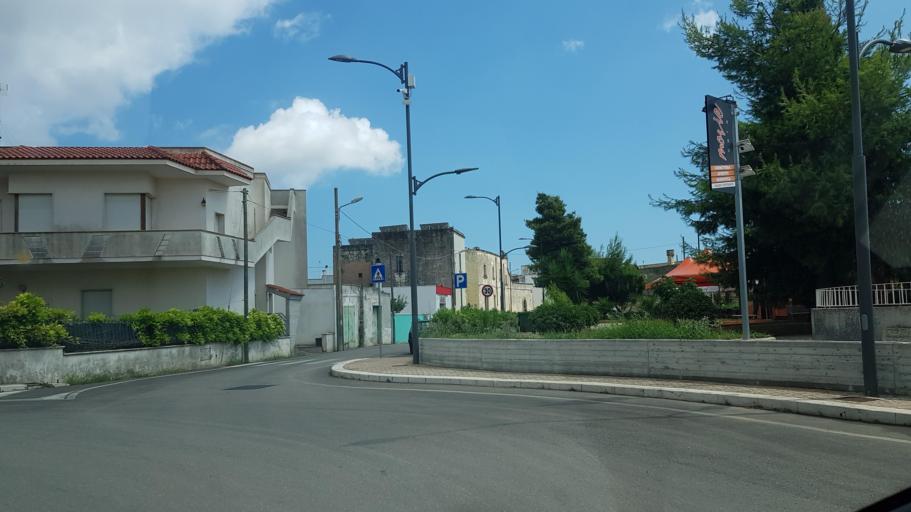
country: IT
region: Apulia
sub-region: Provincia di Lecce
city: Patu
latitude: 39.8432
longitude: 18.3379
